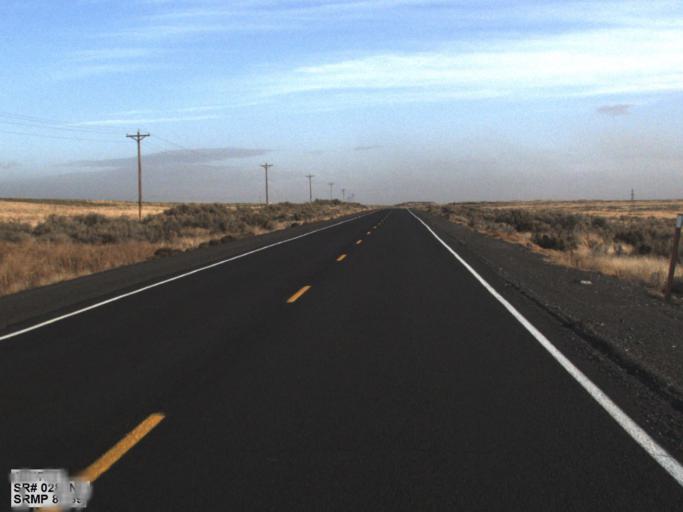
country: US
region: Washington
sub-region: Grant County
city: Warden
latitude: 47.3347
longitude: -118.8913
